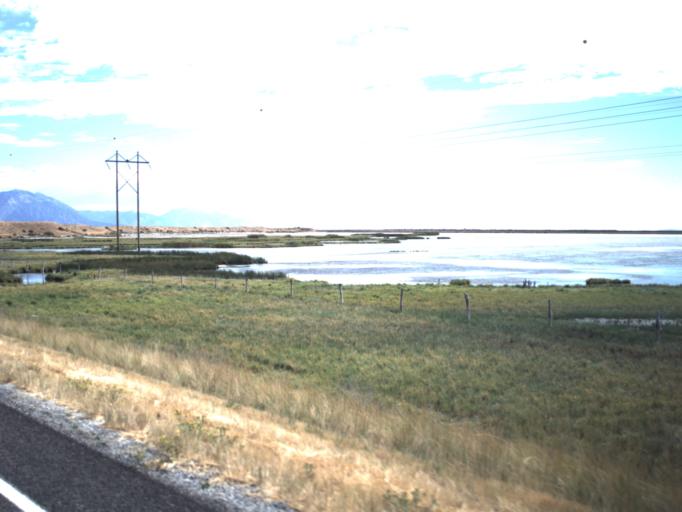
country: US
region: Utah
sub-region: Box Elder County
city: Tremonton
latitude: 41.6040
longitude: -112.3143
